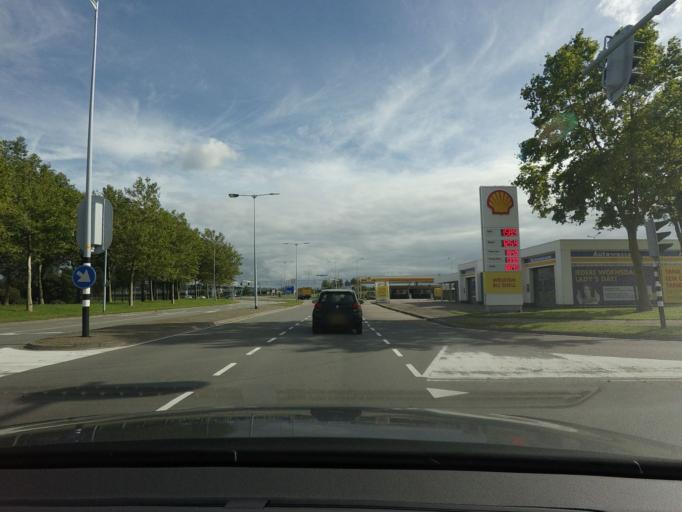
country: NL
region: North Holland
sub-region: Gemeente Haarlemmermeer
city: Hoofddorp
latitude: 52.2919
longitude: 4.6903
